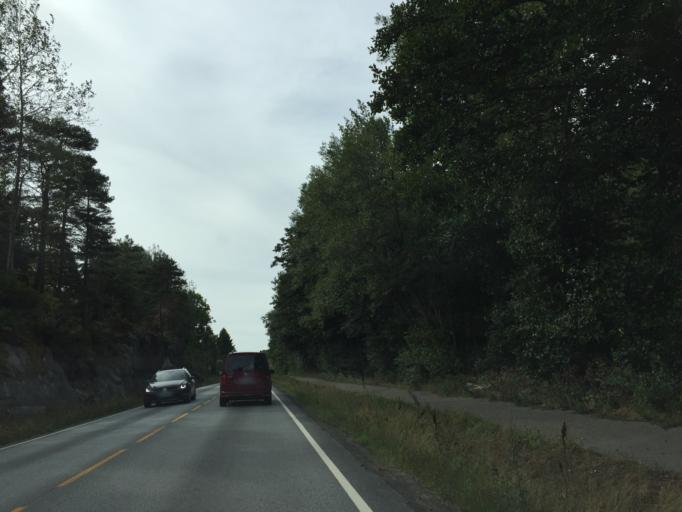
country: NO
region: Ostfold
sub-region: Fredrikstad
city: Fredrikstad
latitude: 59.1093
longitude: 10.9091
